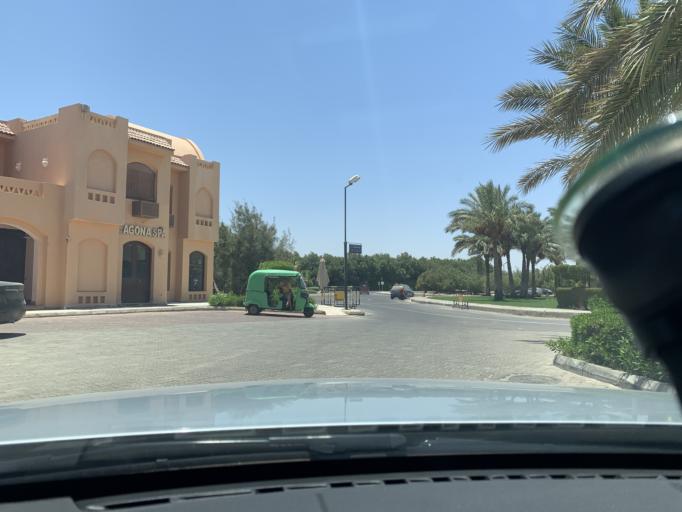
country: EG
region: Red Sea
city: El Gouna
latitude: 27.3951
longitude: 33.6755
